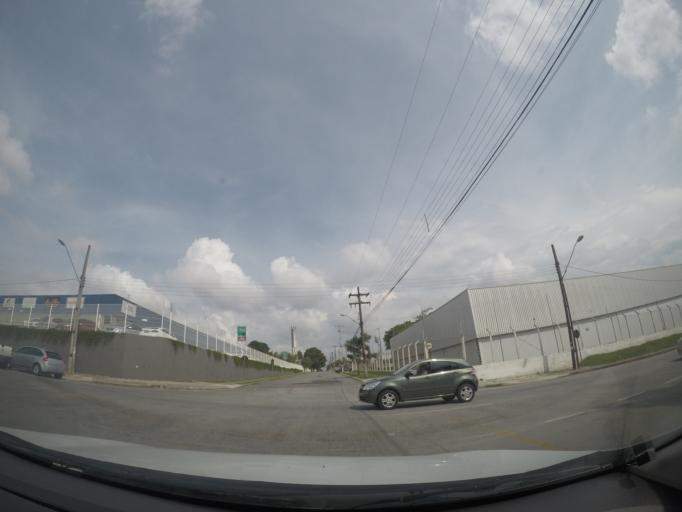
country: BR
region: Parana
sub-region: Curitiba
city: Curitiba
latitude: -25.4847
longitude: -49.2686
